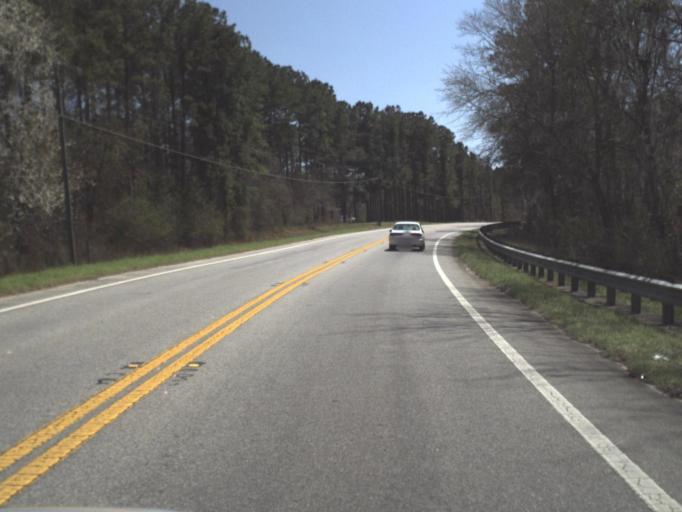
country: US
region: Florida
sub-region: Gadsden County
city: Quincy
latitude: 30.6234
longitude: -84.5953
